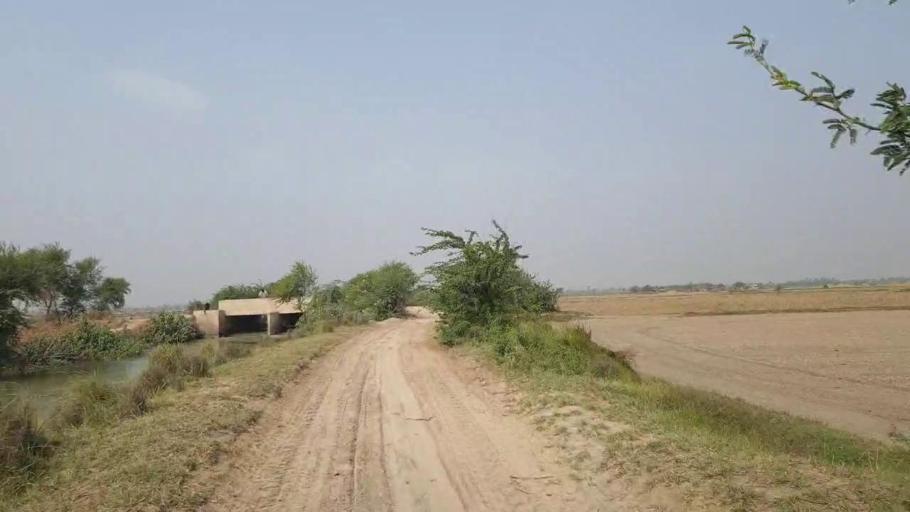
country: PK
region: Sindh
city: Kario
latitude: 24.8518
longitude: 68.5292
